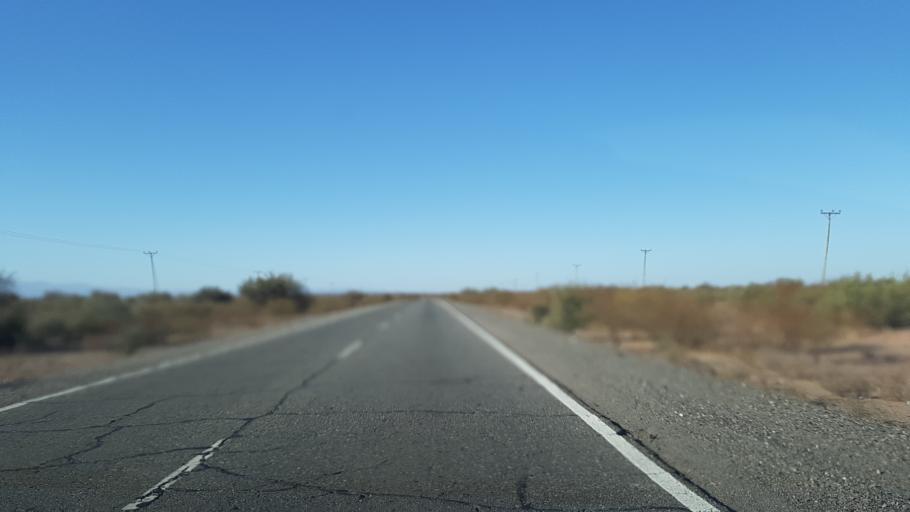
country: AR
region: San Juan
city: Caucete
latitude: -31.6012
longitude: -67.7022
